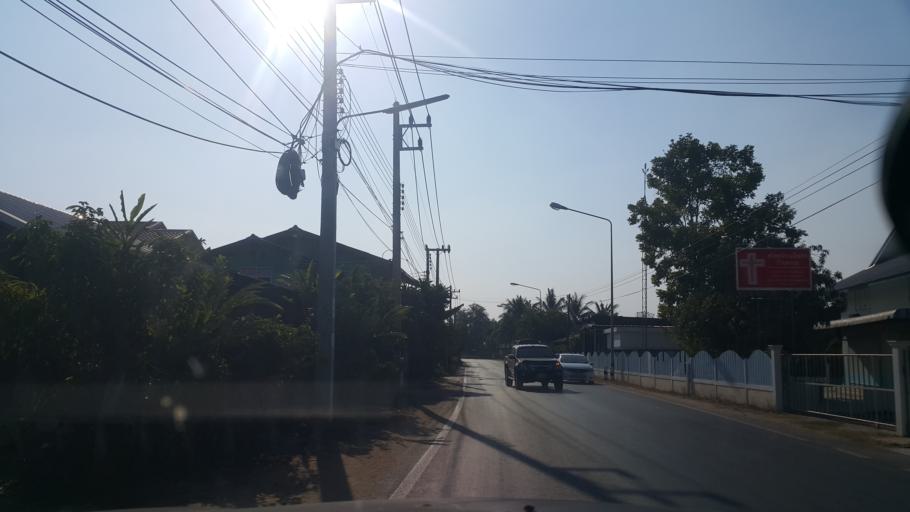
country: TH
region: Nakhon Ratchasima
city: Phimai
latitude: 15.1705
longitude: 102.3966
